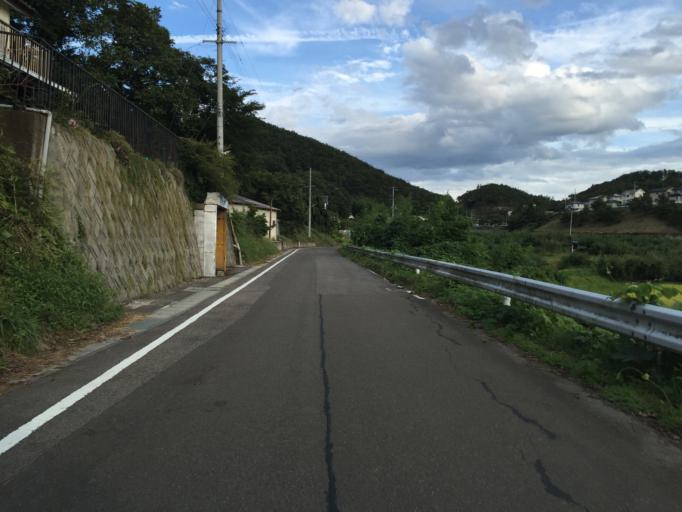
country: JP
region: Fukushima
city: Hobaramachi
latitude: 37.7998
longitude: 140.5132
